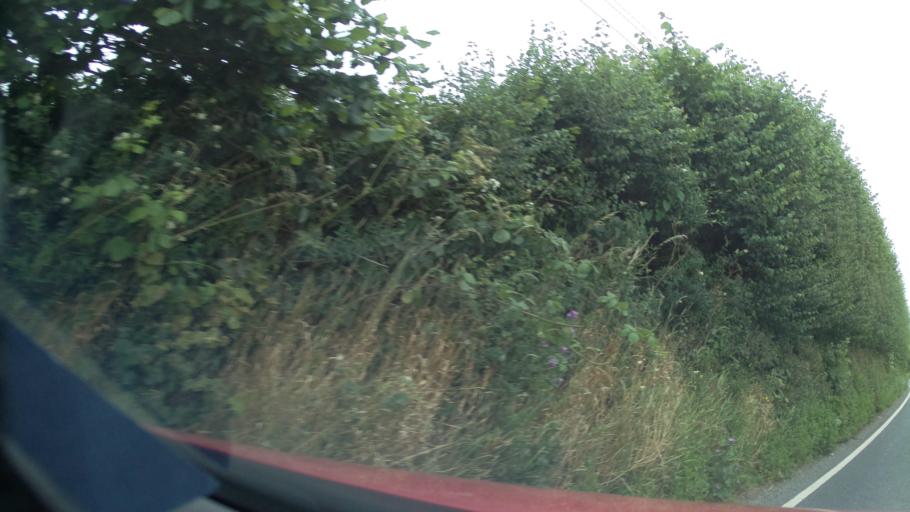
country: GB
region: England
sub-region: Somerset
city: Yeovil
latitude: 50.9219
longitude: -2.6771
